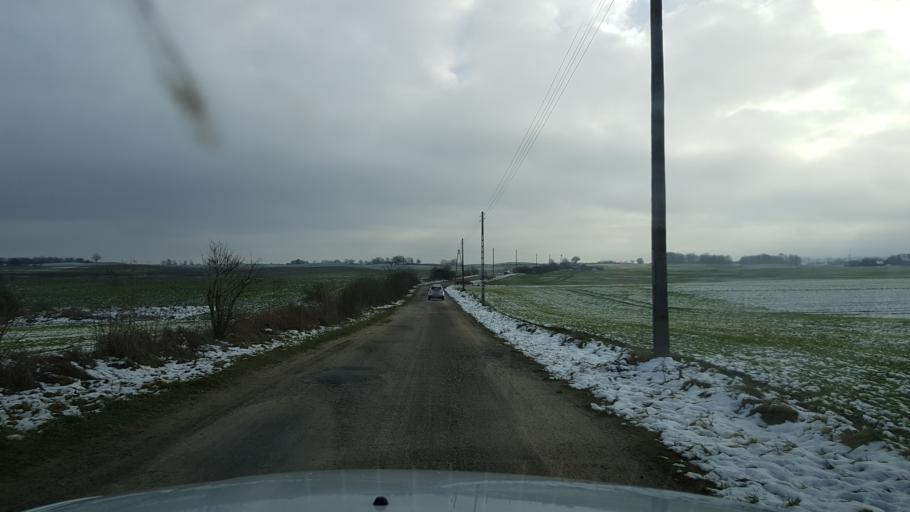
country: PL
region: West Pomeranian Voivodeship
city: Trzcinsko Zdroj
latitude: 52.9579
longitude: 14.6834
